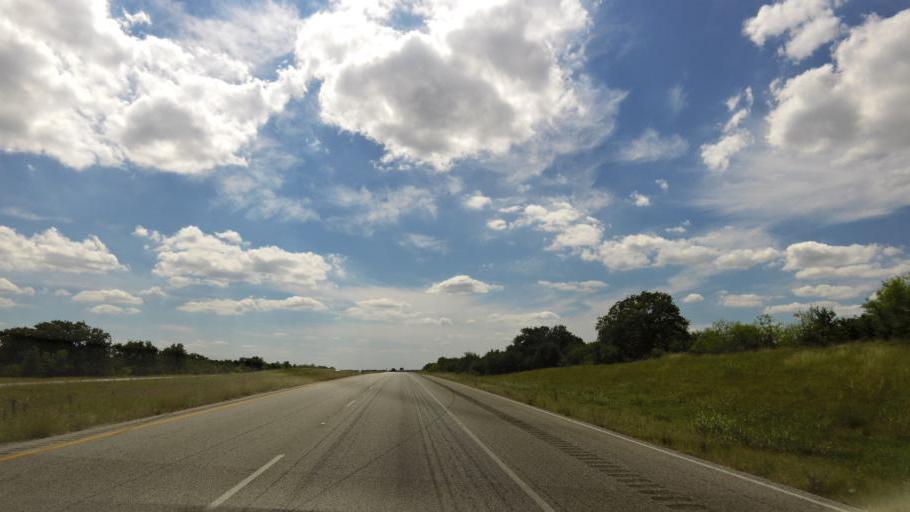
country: US
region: Texas
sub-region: Gonzales County
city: Waelder
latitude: 29.6651
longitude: -97.3542
